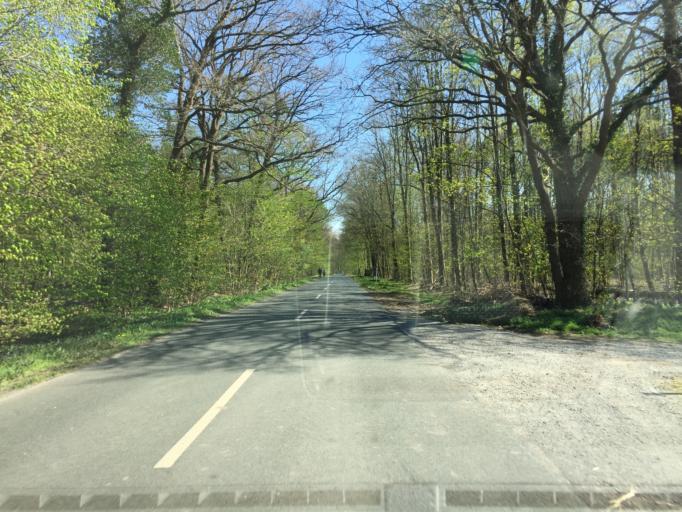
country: DE
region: Lower Saxony
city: Gross Munzel
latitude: 52.4161
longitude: 9.5027
